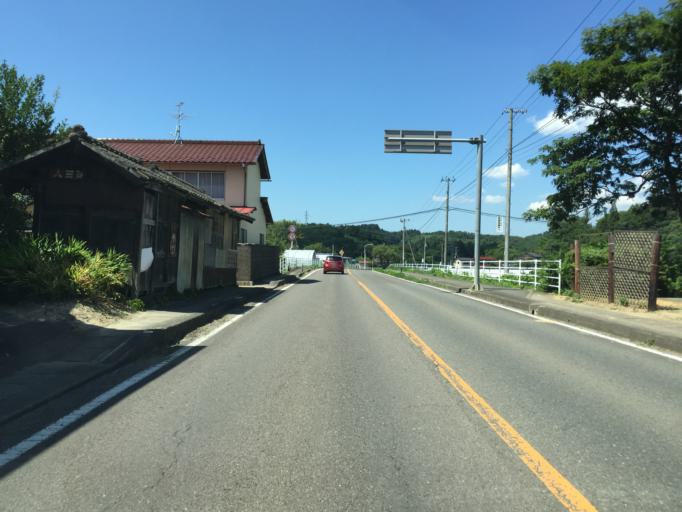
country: JP
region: Fukushima
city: Nihommatsu
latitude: 37.6242
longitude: 140.4615
